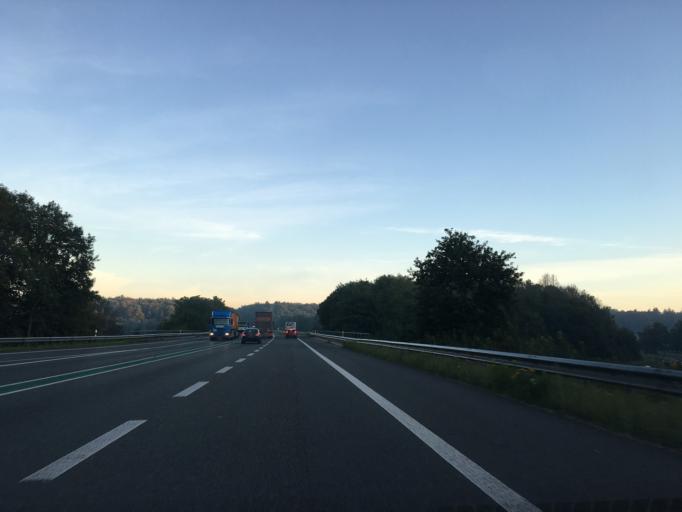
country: DE
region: North Rhine-Westphalia
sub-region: Regierungsbezirk Munster
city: Steinfurt
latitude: 52.1379
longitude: 7.3662
